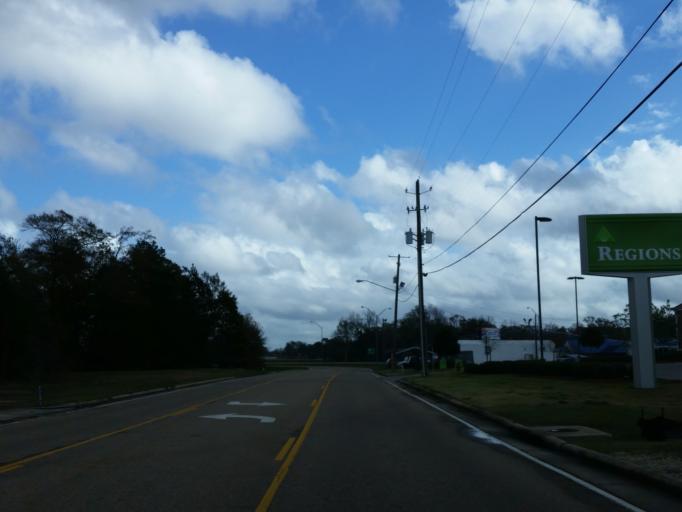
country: US
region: Mississippi
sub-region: Forrest County
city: Hattiesburg
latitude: 31.3052
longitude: -89.3210
